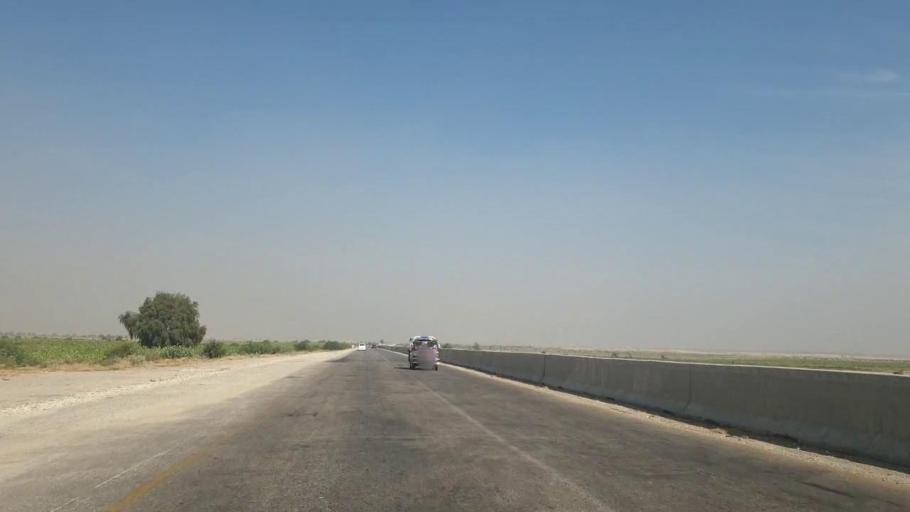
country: PK
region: Sindh
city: Jamshoro
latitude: 25.5388
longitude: 68.2873
